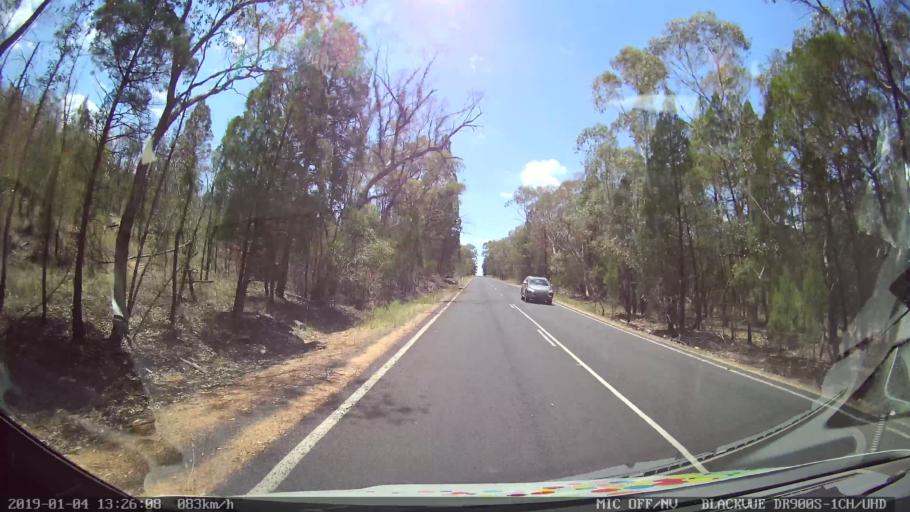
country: AU
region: New South Wales
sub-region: Parkes
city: Peak Hill
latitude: -32.6843
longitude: 148.5559
